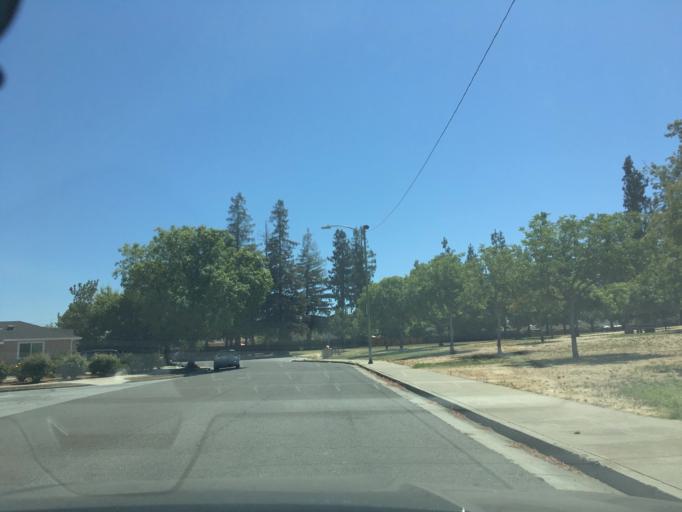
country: US
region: California
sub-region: Santa Clara County
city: Cambrian Park
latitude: 37.2464
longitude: -121.9125
